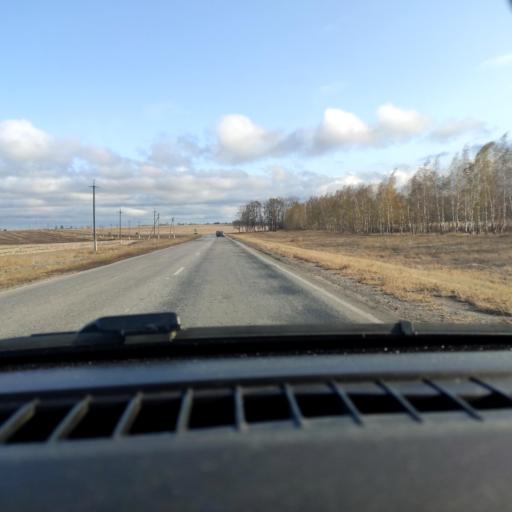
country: RU
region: Belgorod
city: Ilovka
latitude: 50.7160
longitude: 38.6708
